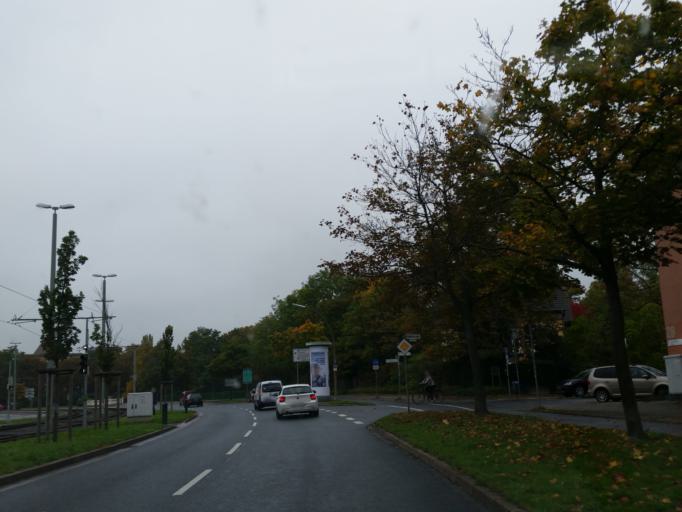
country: DE
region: Lower Saxony
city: Braunschweig
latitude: 52.2578
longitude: 10.5323
